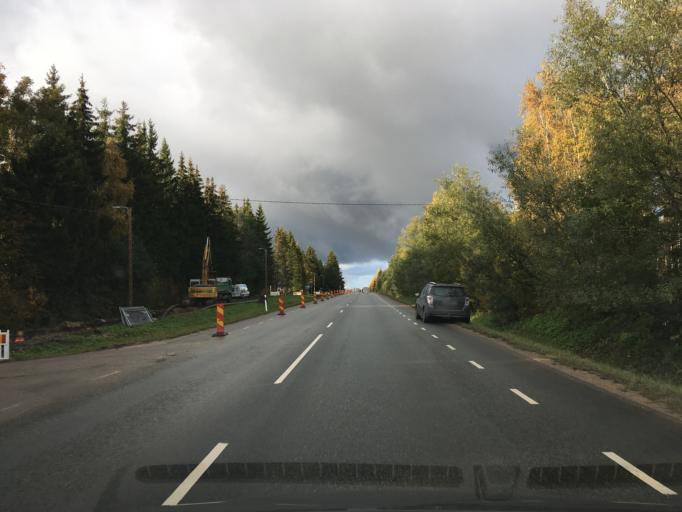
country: EE
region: Harju
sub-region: Saku vald
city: Saku
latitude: 59.2821
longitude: 24.6645
